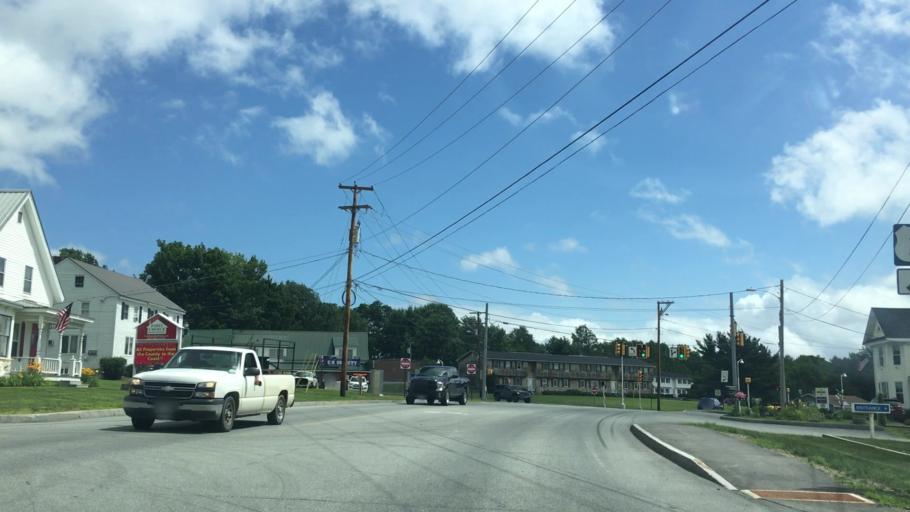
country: US
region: Maine
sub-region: Penobscot County
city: Hermon
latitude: 44.8100
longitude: -68.9128
